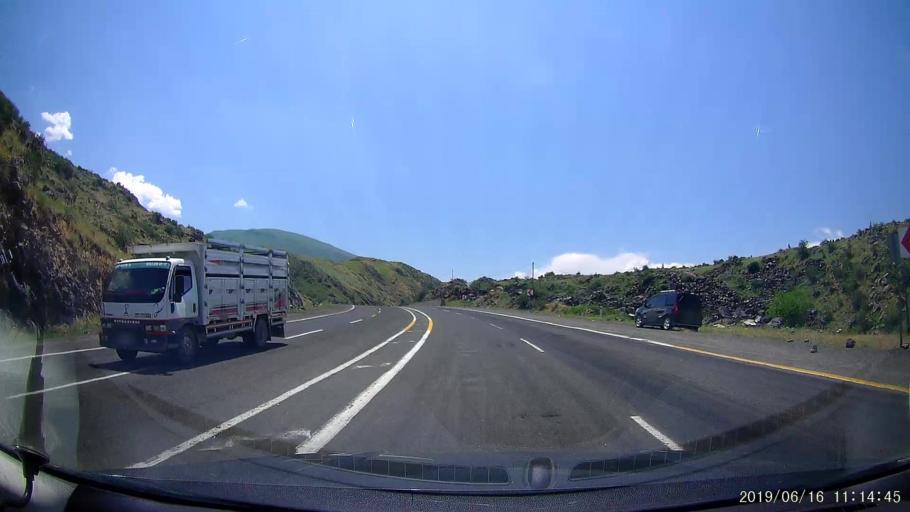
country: TR
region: Igdir
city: Igdir
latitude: 39.7739
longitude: 44.1414
